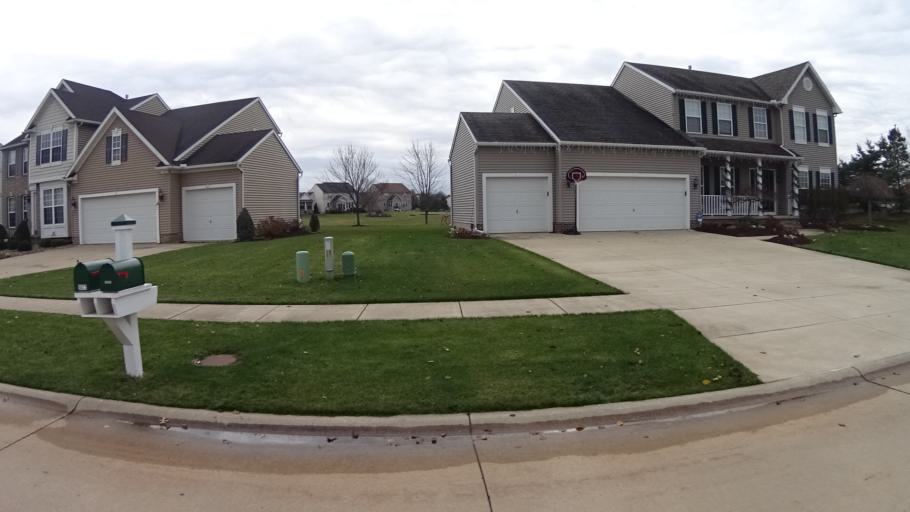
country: US
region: Ohio
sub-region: Lorain County
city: North Ridgeville
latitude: 41.3598
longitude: -82.0396
